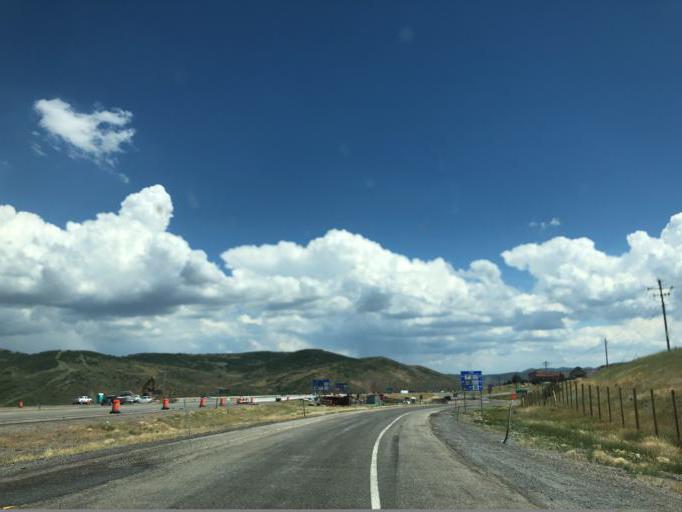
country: US
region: Utah
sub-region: Summit County
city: Summit Park
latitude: 40.7547
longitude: -111.5751
